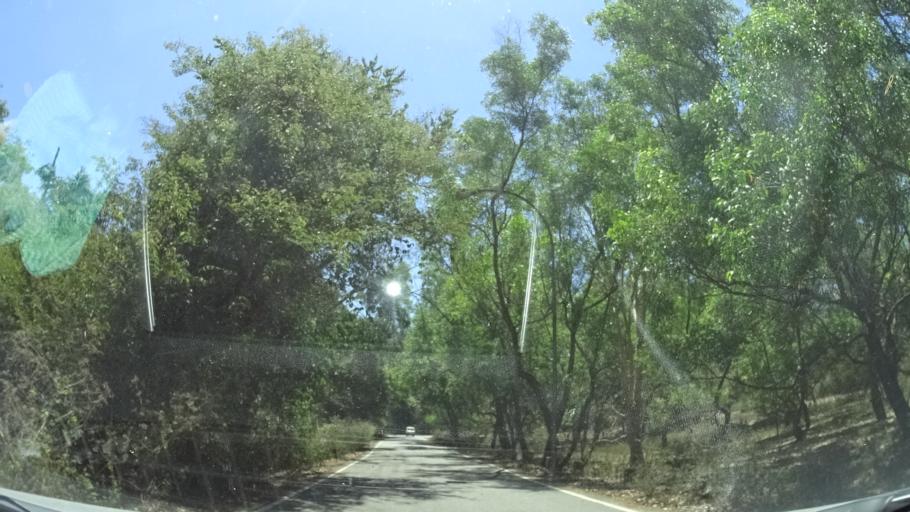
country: IN
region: Karnataka
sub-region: Chikmagalur
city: Sringeri
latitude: 13.2127
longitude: 75.2567
